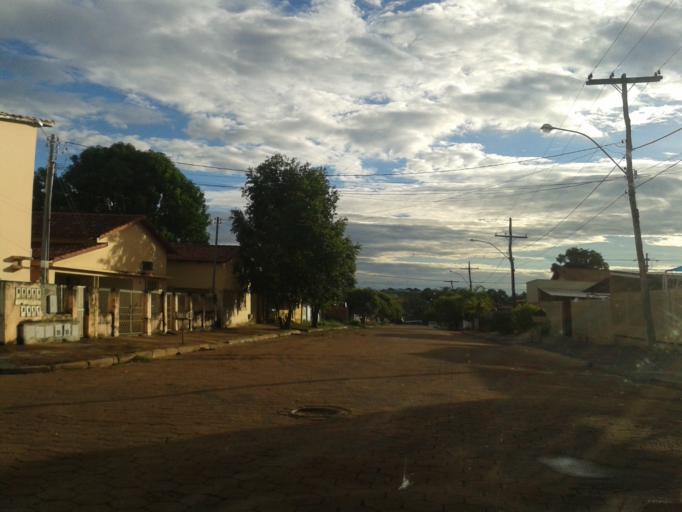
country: BR
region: Goias
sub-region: Sao Miguel Do Araguaia
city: Sao Miguel do Araguaia
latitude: -13.2725
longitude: -50.1615
